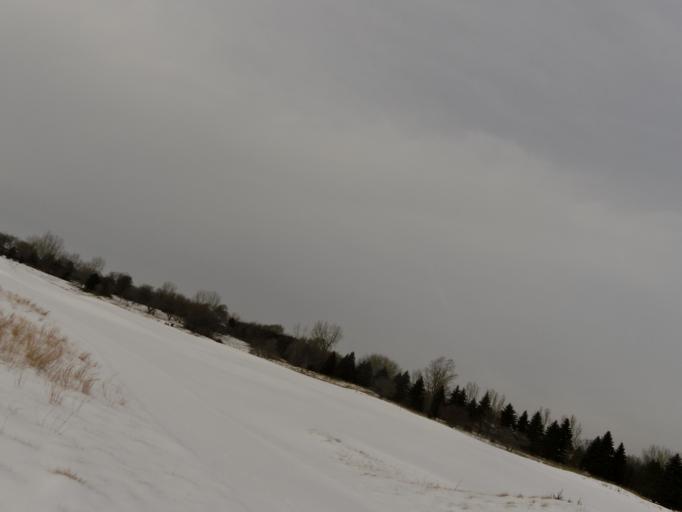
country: US
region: Minnesota
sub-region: Washington County
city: Lakeland
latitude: 44.9567
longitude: -92.8250
